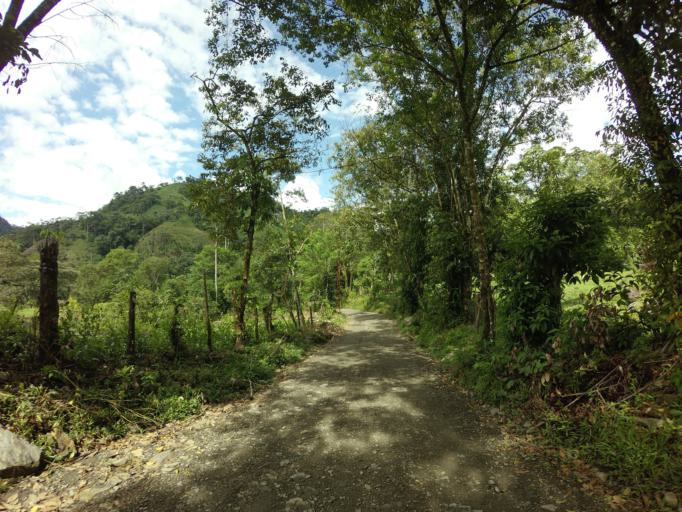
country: CO
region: Antioquia
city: Narino
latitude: 5.5407
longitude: -75.1308
